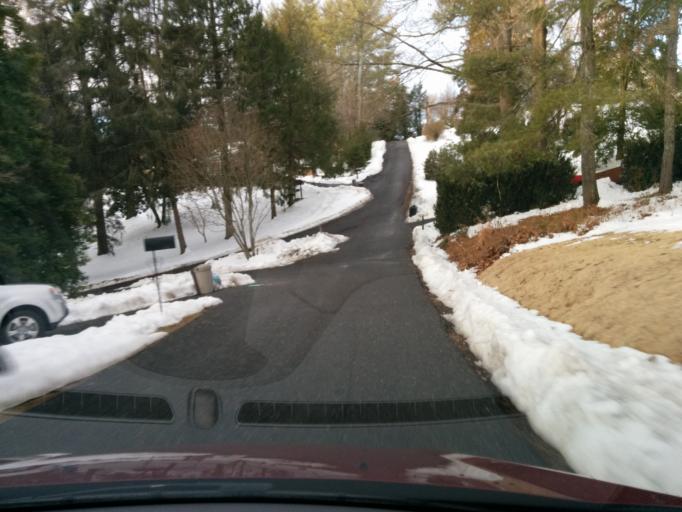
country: US
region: Virginia
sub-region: City of Lexington
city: Lexington
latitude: 37.7838
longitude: -79.4532
